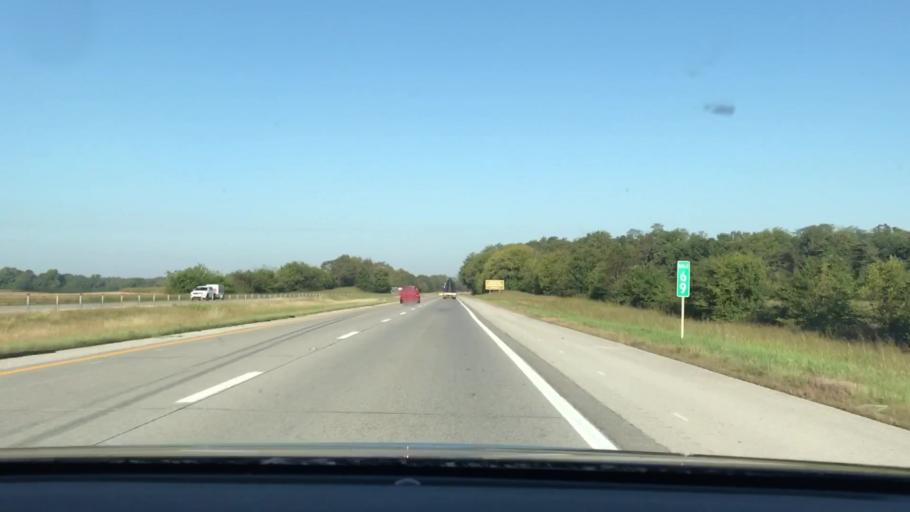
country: US
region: Kentucky
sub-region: Trigg County
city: Cadiz
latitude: 36.8497
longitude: -87.6900
